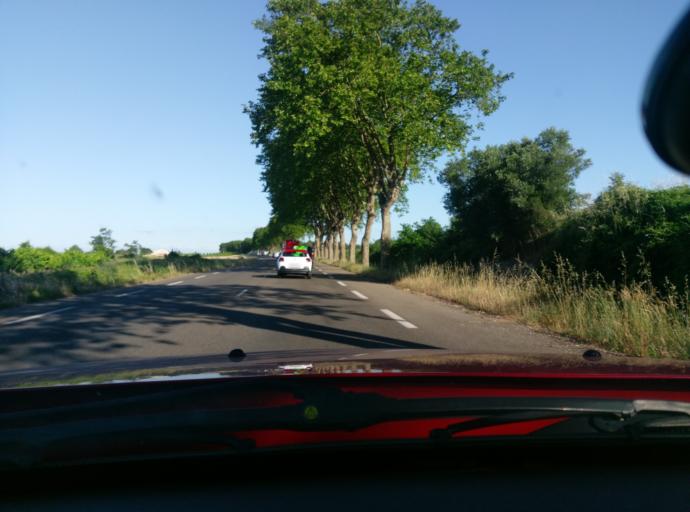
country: FR
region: Languedoc-Roussillon
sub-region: Departement du Gard
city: Uzes
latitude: 43.9840
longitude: 4.4624
